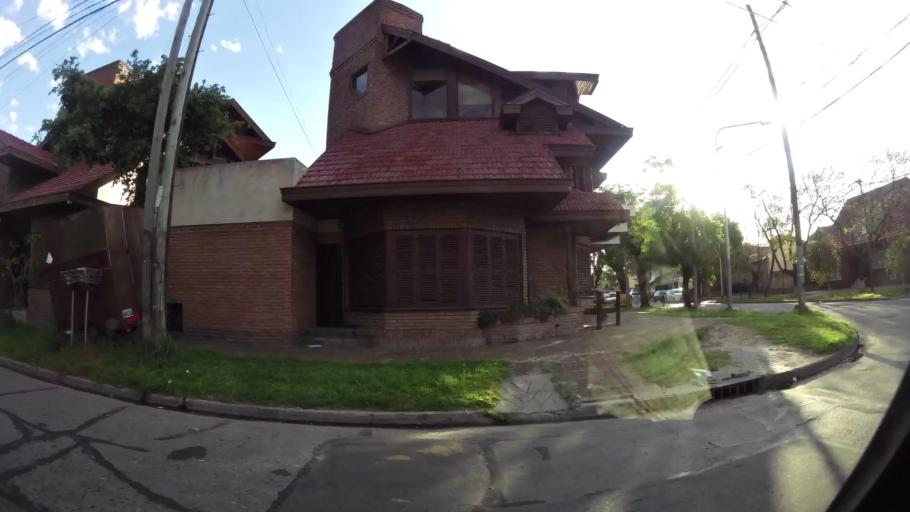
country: AR
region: Buenos Aires
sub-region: Partido de Avellaneda
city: Avellaneda
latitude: -34.6811
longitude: -58.3487
